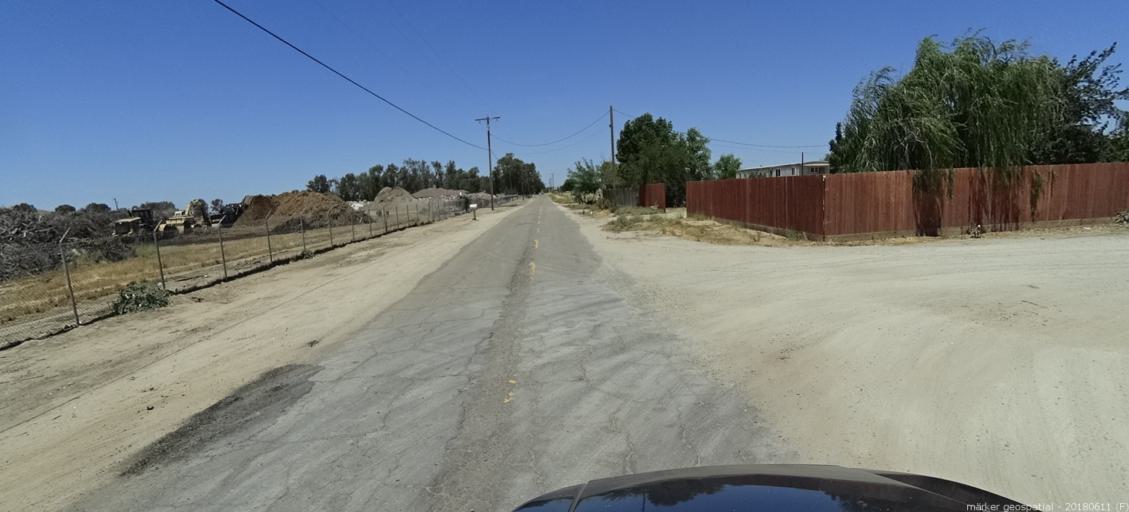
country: US
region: California
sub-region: Madera County
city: Fairmead
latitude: 37.0646
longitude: -120.1934
